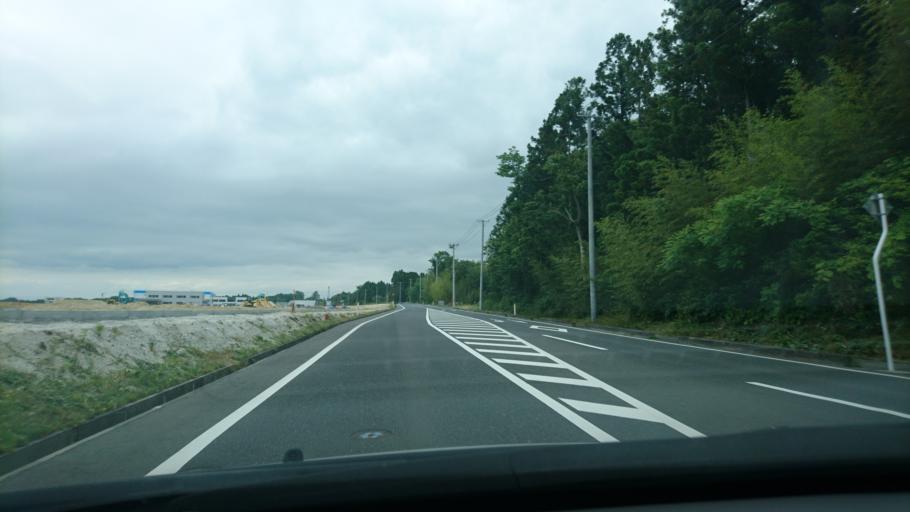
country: JP
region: Miyagi
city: Kogota
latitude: 38.7198
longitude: 141.0394
